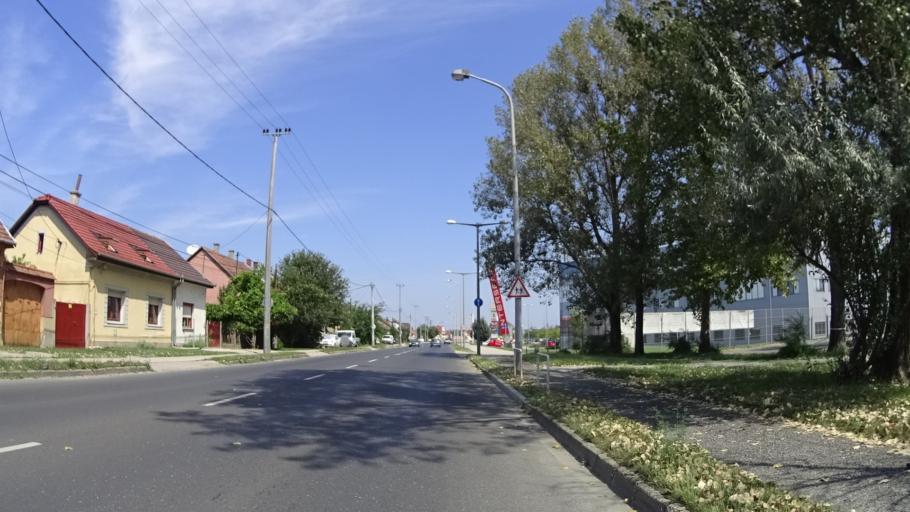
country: HU
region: Fejer
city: Szekesfehervar
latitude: 47.1635
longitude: 18.4025
